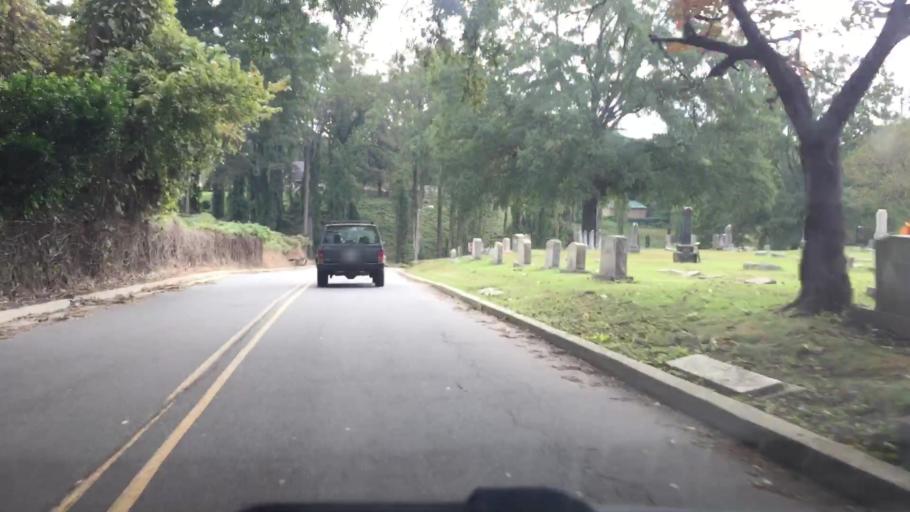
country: US
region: North Carolina
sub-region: Iredell County
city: Mooresville
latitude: 35.5799
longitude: -80.8116
